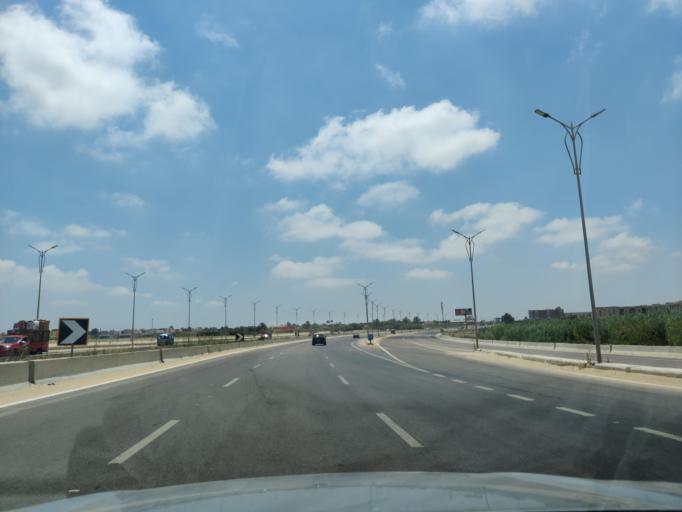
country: EG
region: Alexandria
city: Alexandria
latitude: 30.9856
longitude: 29.6576
